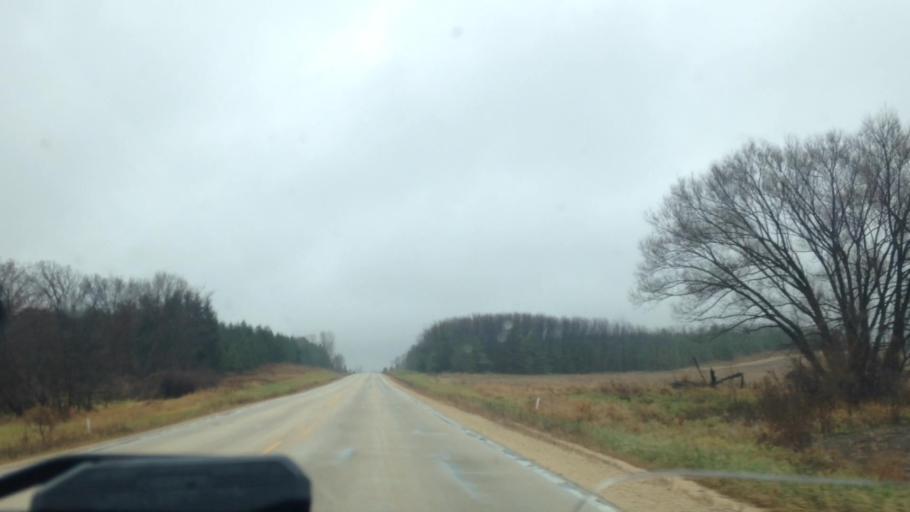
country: US
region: Wisconsin
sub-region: Dodge County
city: Mayville
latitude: 43.4913
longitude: -88.5194
